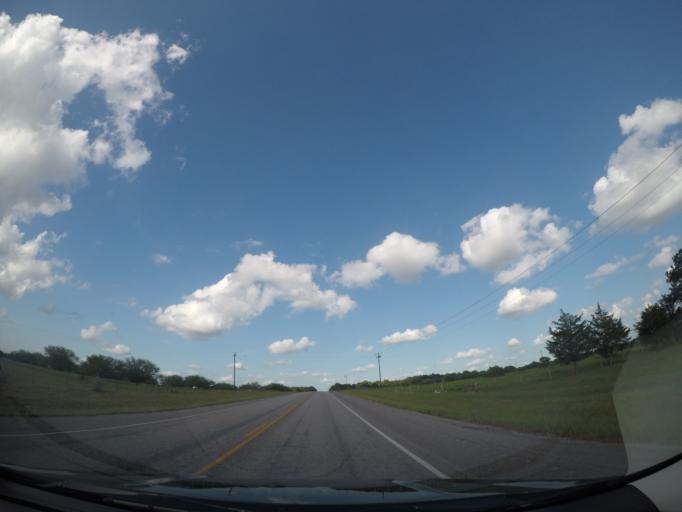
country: US
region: Texas
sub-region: Lavaca County
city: Hallettsville
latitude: 29.4785
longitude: -96.7728
